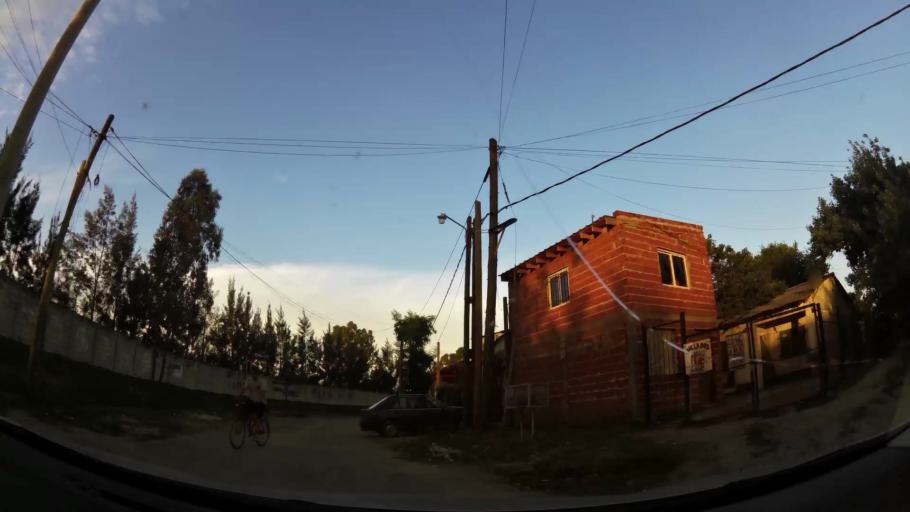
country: AR
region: Buenos Aires
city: Santa Catalina - Dique Lujan
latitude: -34.4384
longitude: -58.6646
